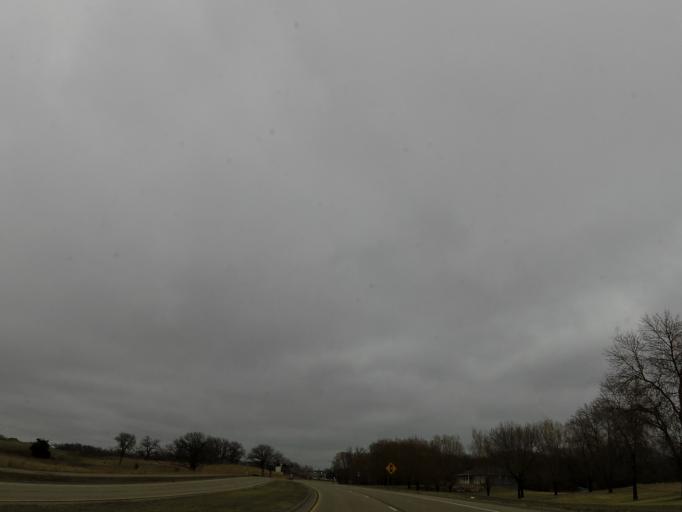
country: US
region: Minnesota
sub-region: Scott County
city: Prior Lake
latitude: 44.7235
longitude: -93.4717
